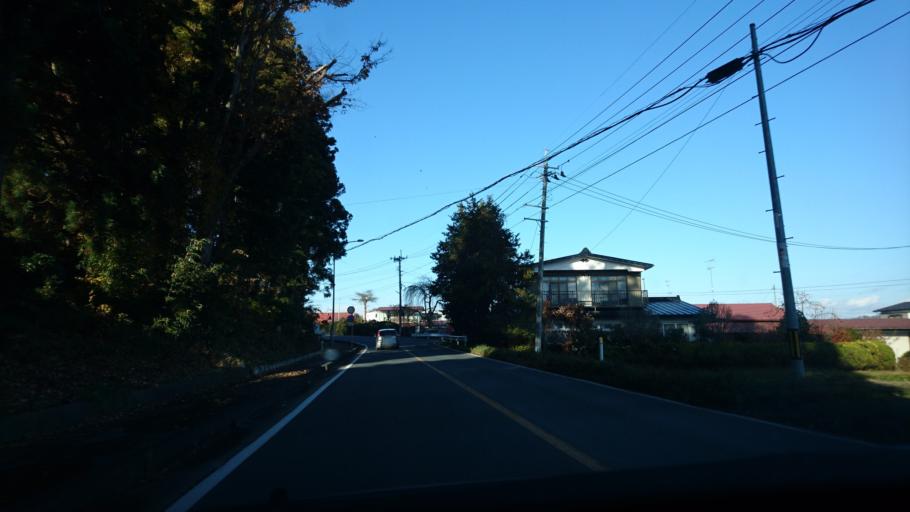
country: JP
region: Iwate
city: Mizusawa
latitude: 39.1214
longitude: 141.1647
